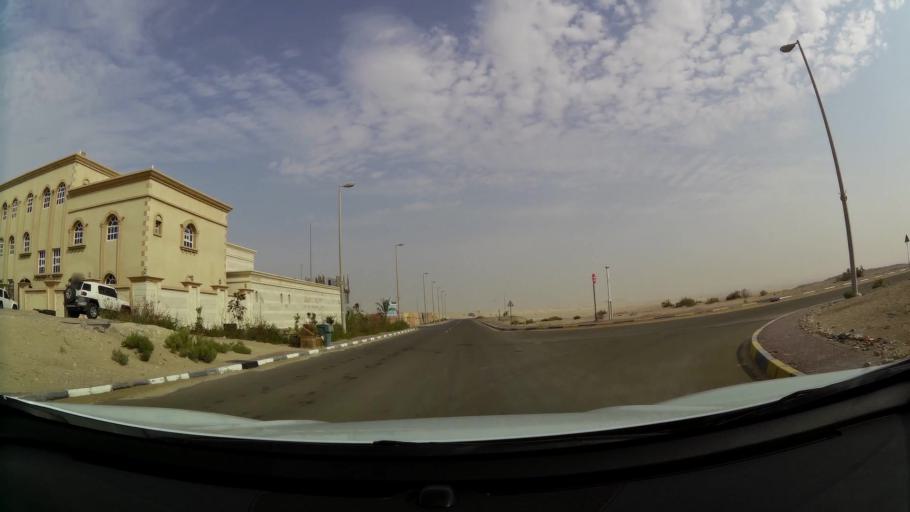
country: AE
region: Abu Dhabi
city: Abu Dhabi
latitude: 24.2551
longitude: 54.7220
